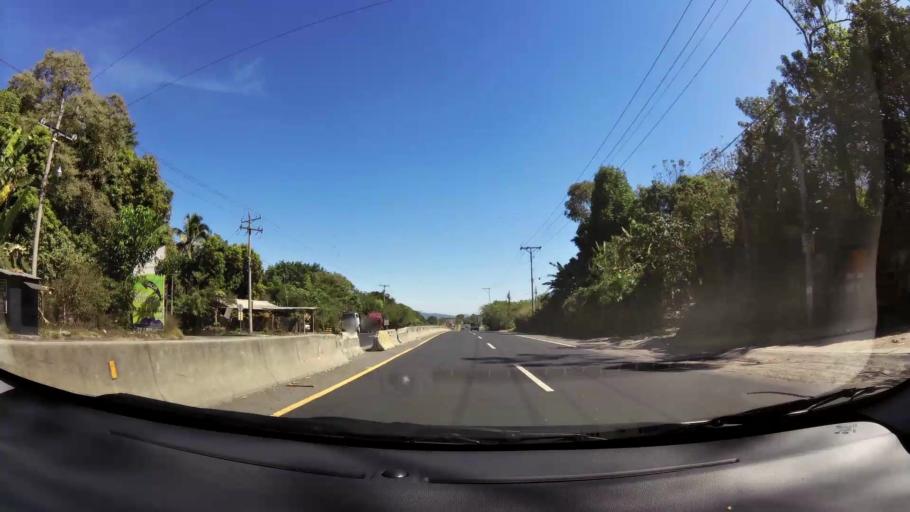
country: SV
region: La Libertad
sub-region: Distrito de Quezaltepeque
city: Quezaltepeque
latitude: 13.8221
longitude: -89.2816
